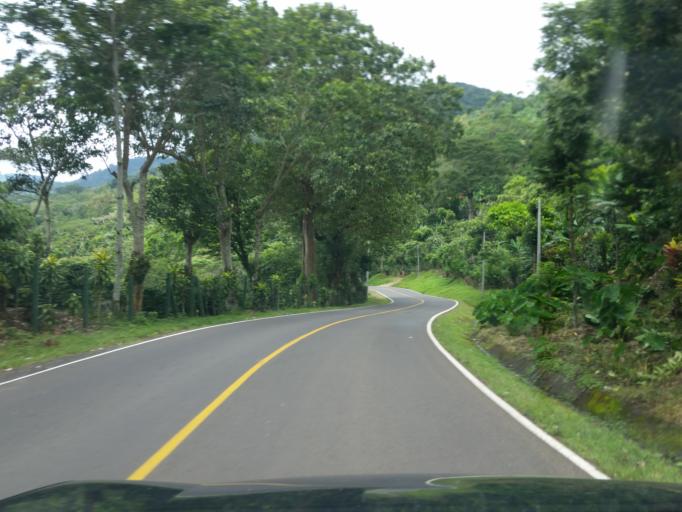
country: NI
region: Matagalpa
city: San Ramon
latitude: 12.9612
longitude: -85.8635
